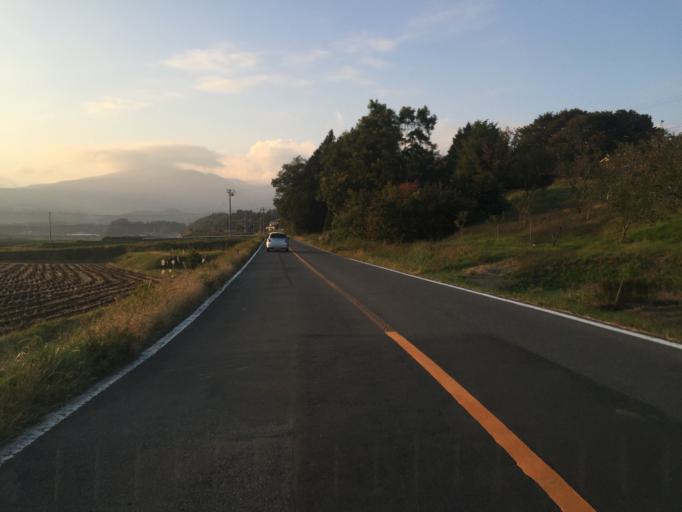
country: JP
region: Fukushima
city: Motomiya
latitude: 37.5478
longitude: 140.3673
